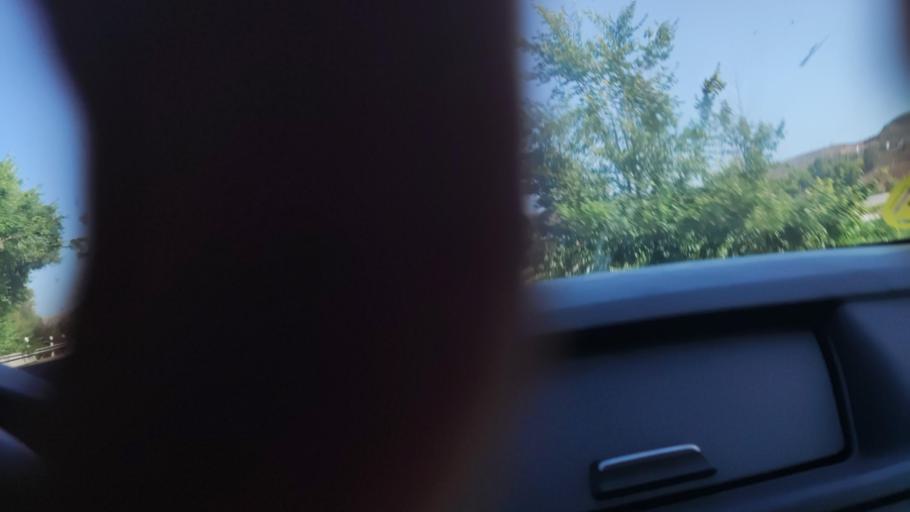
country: ES
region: Castille-La Mancha
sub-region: Provincia de Albacete
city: Hellin
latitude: 38.4933
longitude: -1.6412
